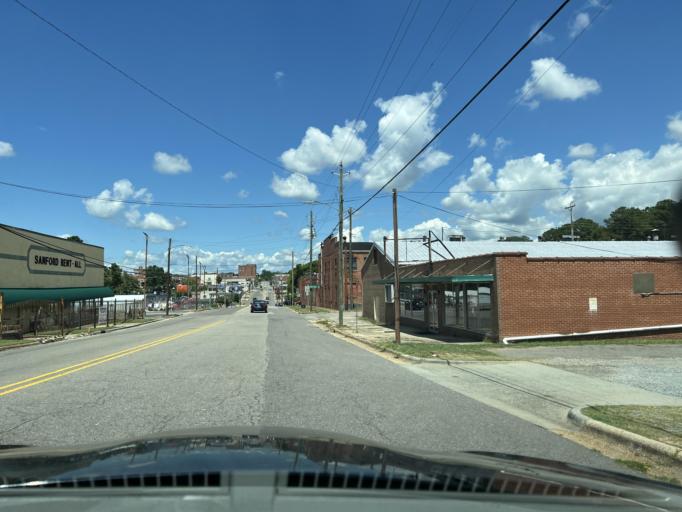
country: US
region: North Carolina
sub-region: Lee County
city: Sanford
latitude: 35.4758
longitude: -79.1845
